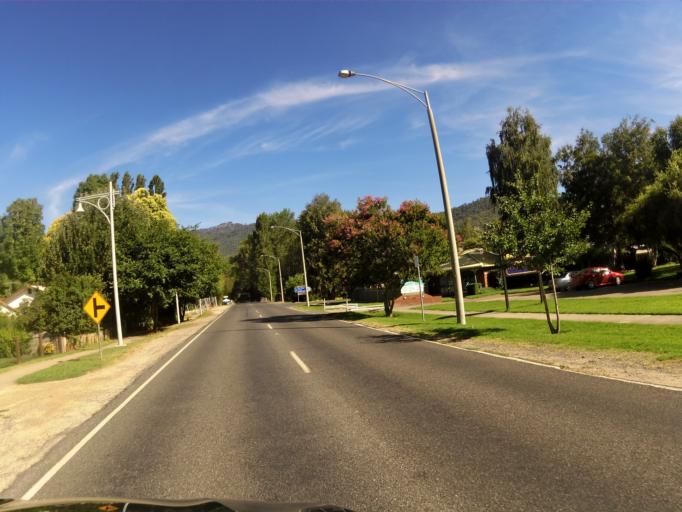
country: AU
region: Victoria
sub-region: Alpine
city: Mount Beauty
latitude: -36.7386
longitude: 147.1617
